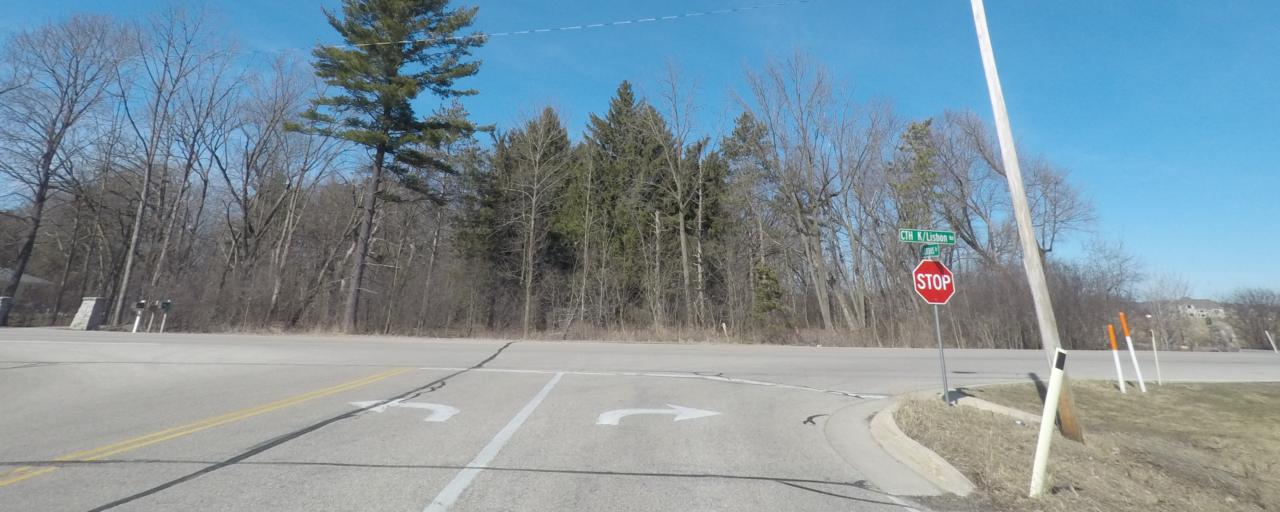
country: US
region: Wisconsin
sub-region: Waukesha County
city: Hartland
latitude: 43.1196
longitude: -88.3522
